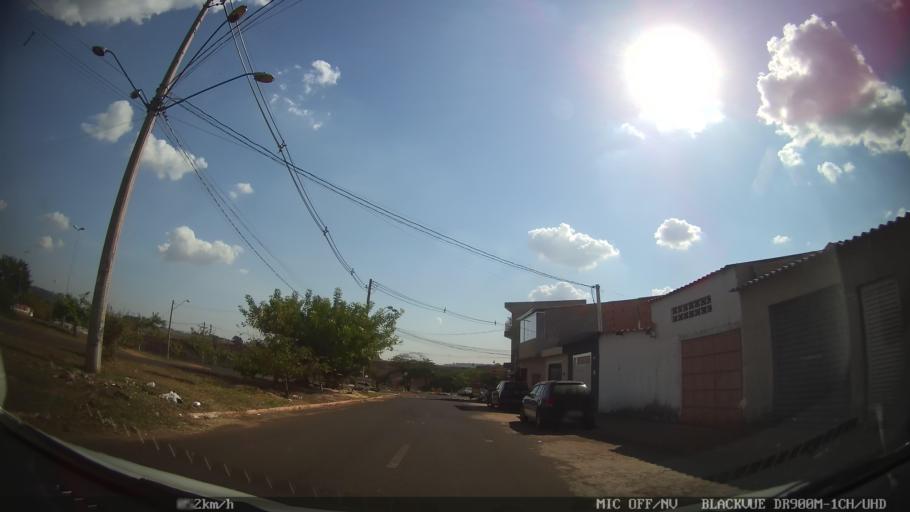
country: BR
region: Sao Paulo
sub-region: Ribeirao Preto
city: Ribeirao Preto
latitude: -21.2019
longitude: -47.8568
